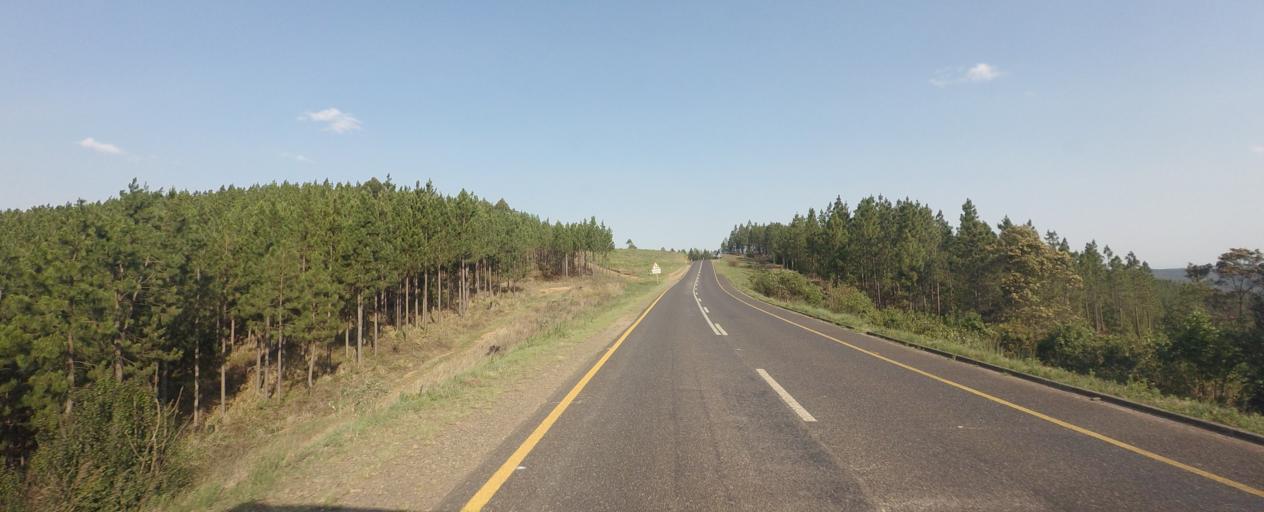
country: ZA
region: Mpumalanga
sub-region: Ehlanzeni District
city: Lydenburg
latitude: -25.1794
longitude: 30.6968
